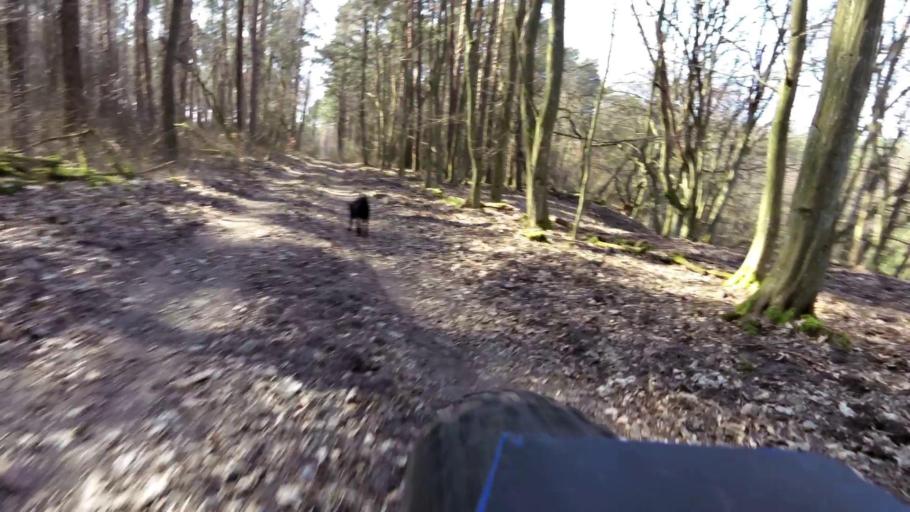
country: PL
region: Lubusz
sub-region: Powiat slubicki
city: Cybinka
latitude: 52.2054
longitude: 14.8993
